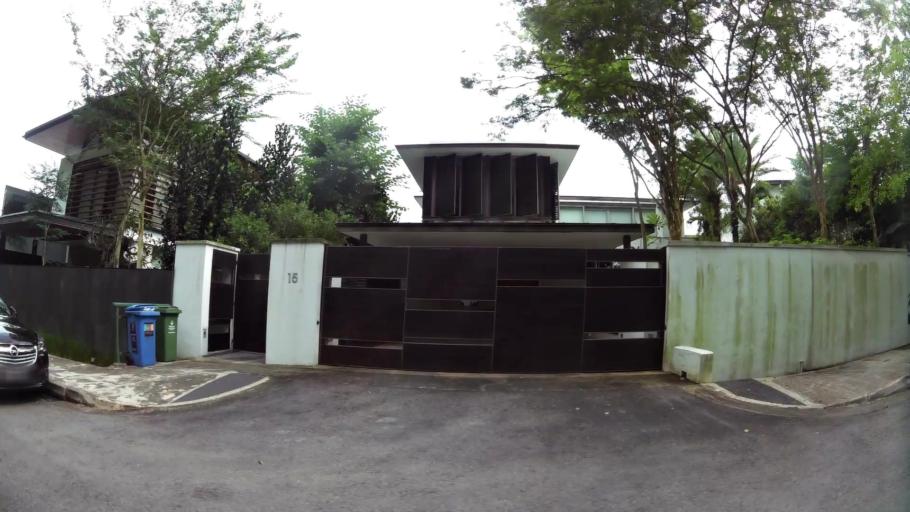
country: SG
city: Singapore
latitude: 1.3365
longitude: 103.8067
